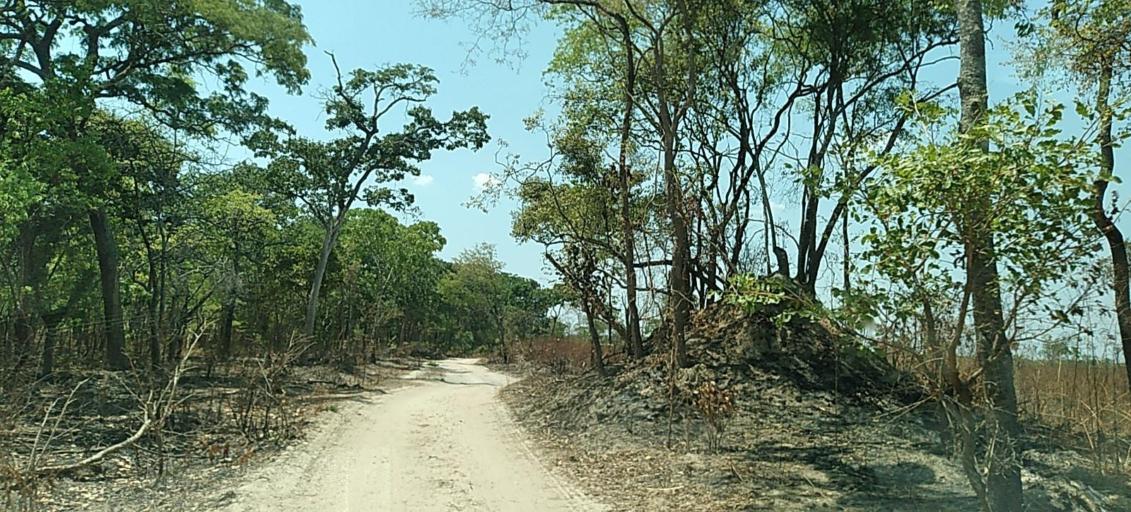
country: ZM
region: Copperbelt
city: Mpongwe
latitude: -13.6336
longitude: 28.4803
